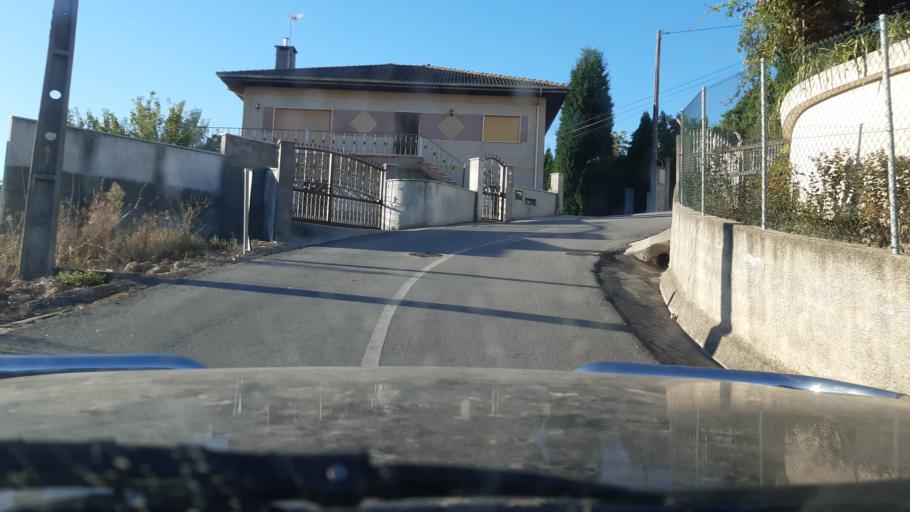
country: PT
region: Aveiro
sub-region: Agueda
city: Agueda
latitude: 40.5800
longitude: -8.4557
